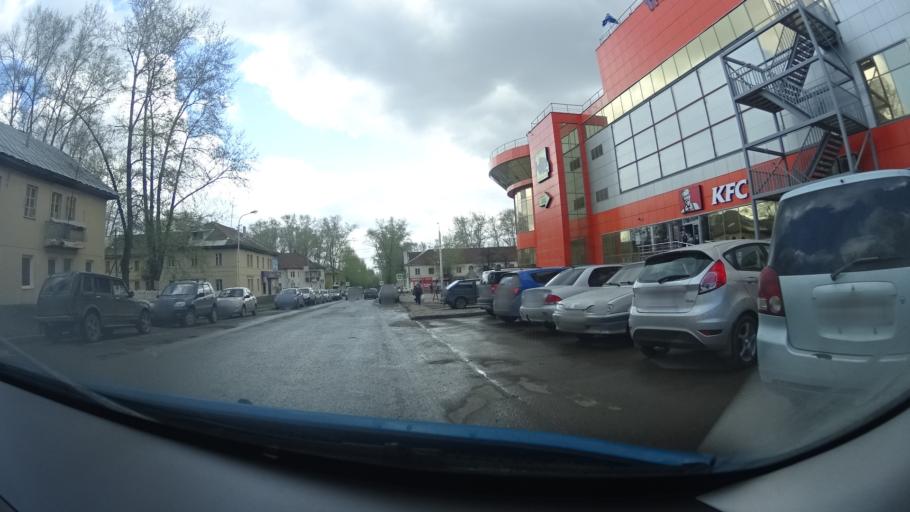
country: RU
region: Bashkortostan
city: Ufa
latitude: 54.8226
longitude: 56.0860
